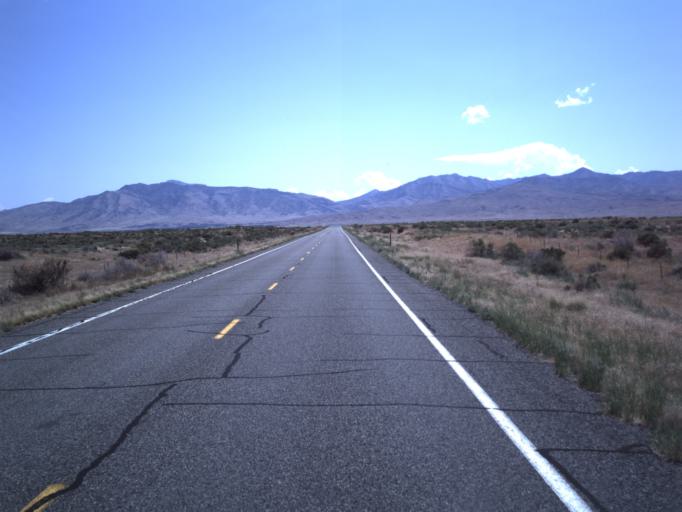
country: US
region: Utah
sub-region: Millard County
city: Delta
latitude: 39.3534
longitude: -112.4854
